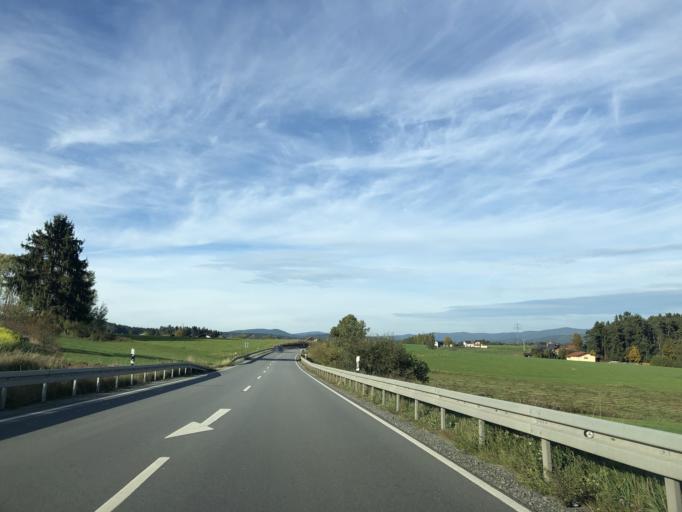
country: DE
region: Bavaria
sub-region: Lower Bavaria
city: Ruhmannsfelden
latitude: 48.9904
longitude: 12.9800
